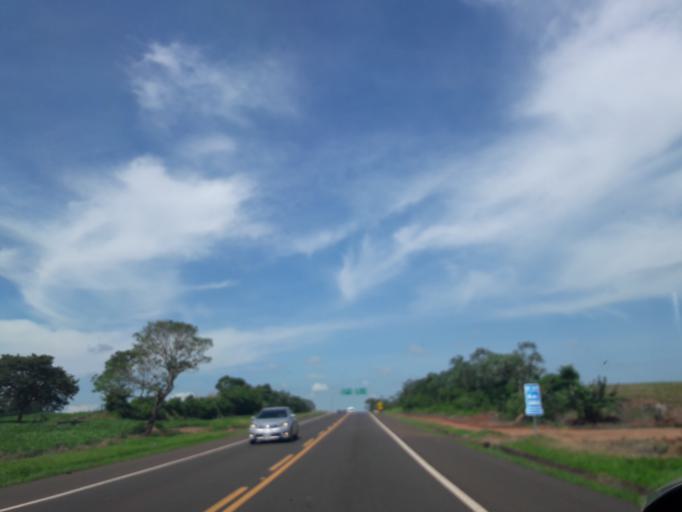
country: BR
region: Parana
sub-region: Campo Mourao
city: Campo Mourao
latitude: -24.2799
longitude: -52.5350
